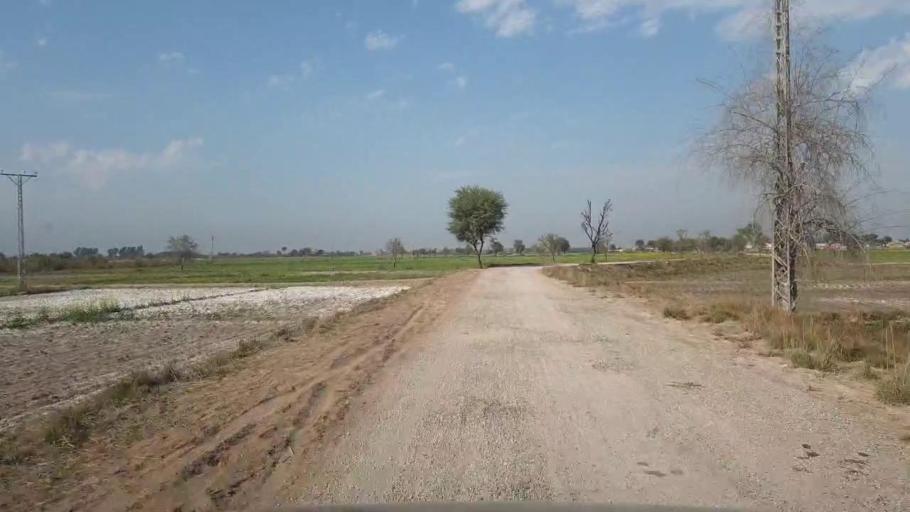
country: PK
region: Sindh
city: Sakrand
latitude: 26.0170
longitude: 68.4168
